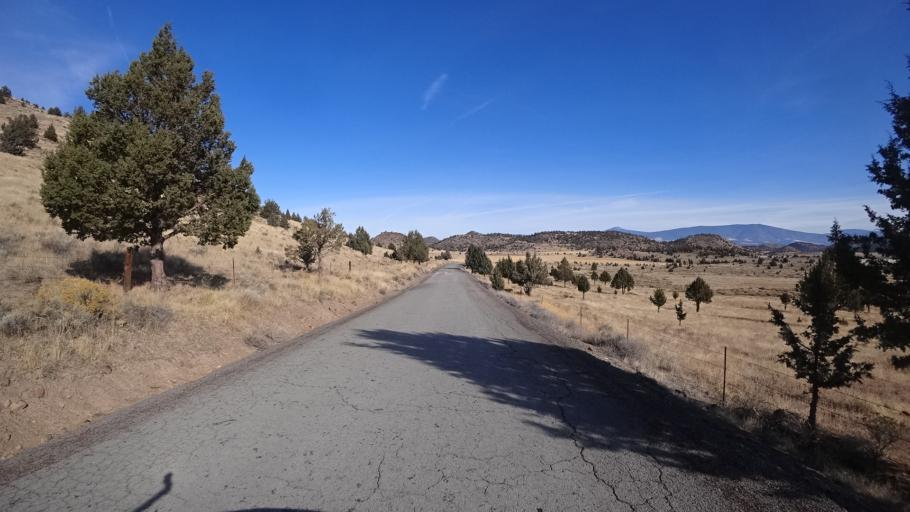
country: US
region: California
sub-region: Siskiyou County
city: Weed
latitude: 41.5555
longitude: -122.4731
